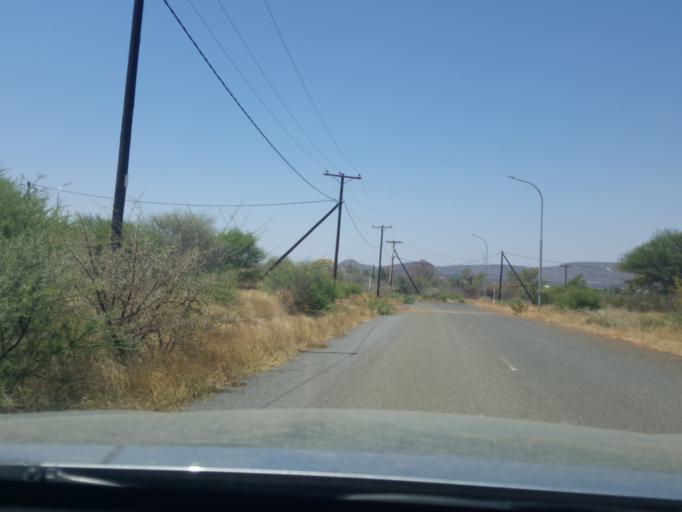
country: BW
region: South East
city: Lobatse
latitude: -25.1904
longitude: 25.6745
